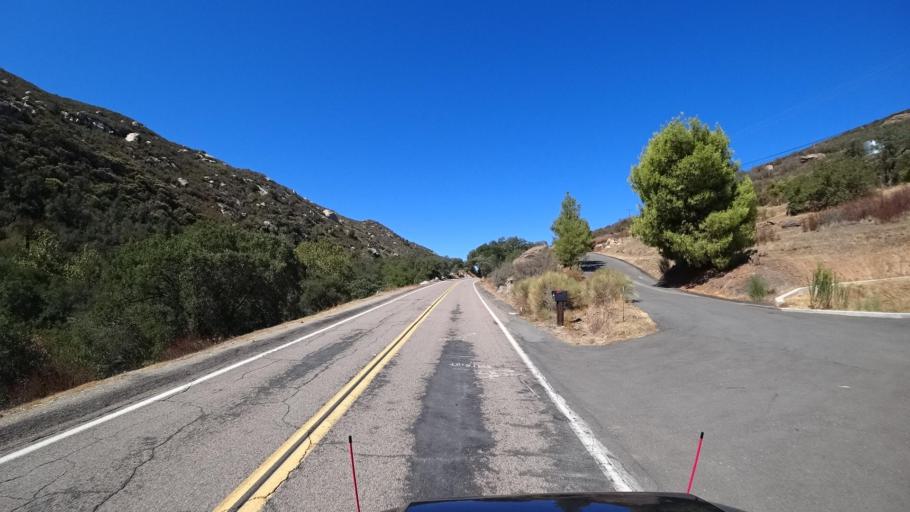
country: US
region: California
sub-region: San Diego County
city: Alpine
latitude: 32.7051
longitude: -116.7299
